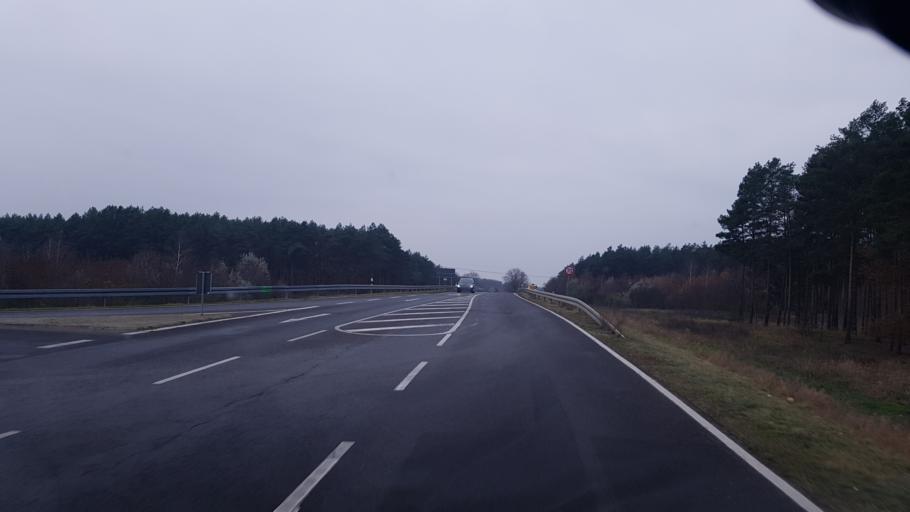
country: DE
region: Brandenburg
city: Schenkendobern
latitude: 51.9545
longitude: 14.6483
